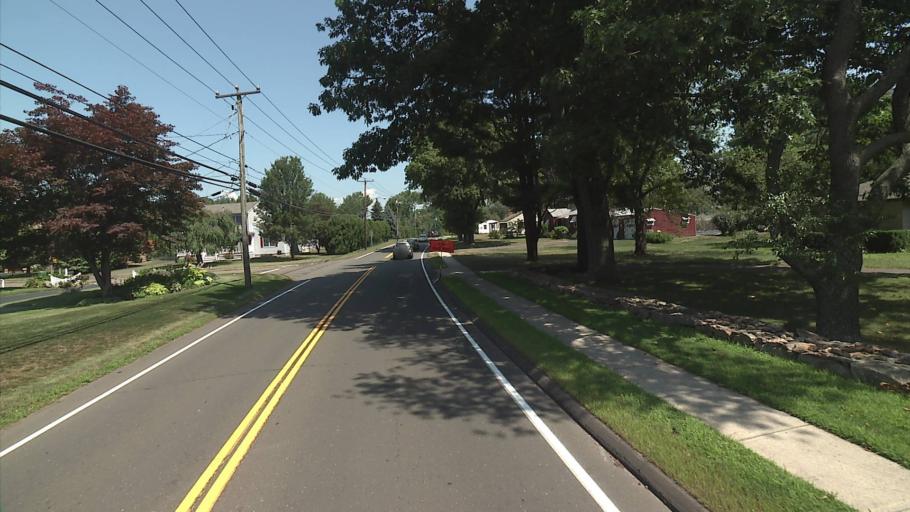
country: US
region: Connecticut
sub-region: New Haven County
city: Branford Center
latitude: 41.2699
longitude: -72.8314
